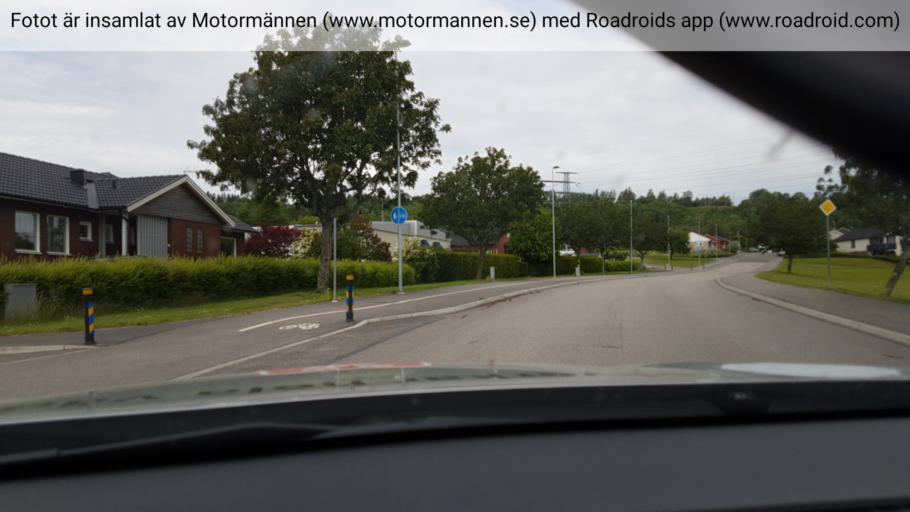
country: SE
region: Vaestra Goetaland
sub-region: Falkopings Kommun
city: Falkoeping
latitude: 58.1693
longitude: 13.5330
